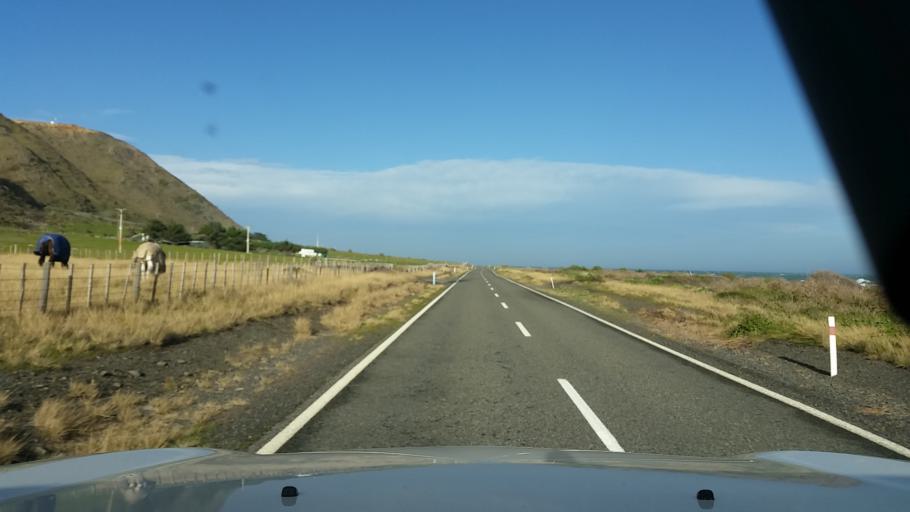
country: NZ
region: Wellington
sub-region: South Wairarapa District
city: Waipawa
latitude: -41.5135
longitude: 175.2019
